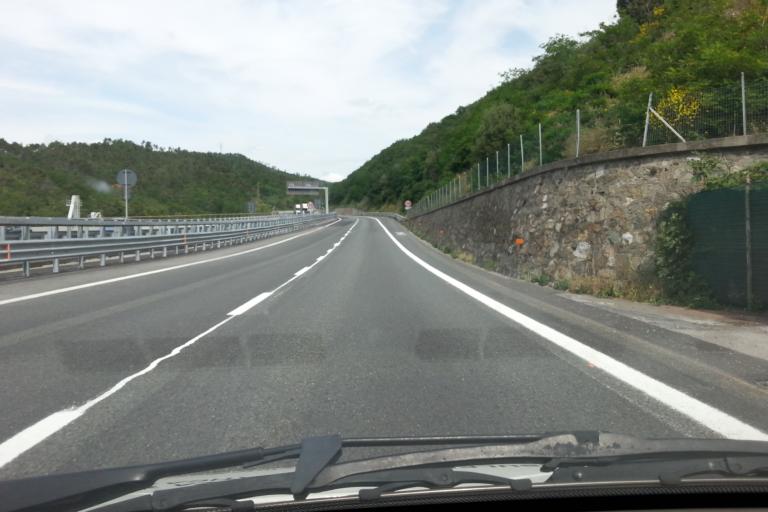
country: IT
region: Liguria
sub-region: Provincia di Savona
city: Valleggia
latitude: 44.2909
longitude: 8.4396
